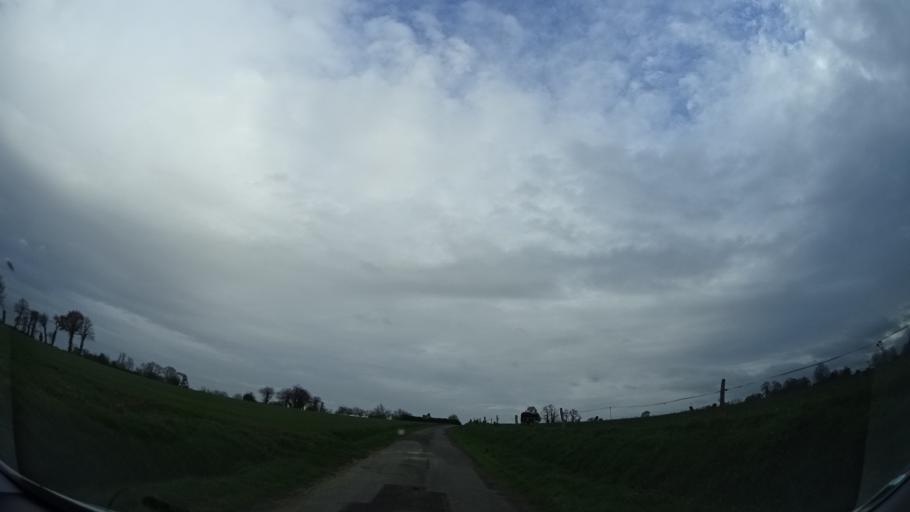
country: FR
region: Brittany
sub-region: Departement des Cotes-d'Armor
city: Evran
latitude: 48.3339
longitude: -1.9529
